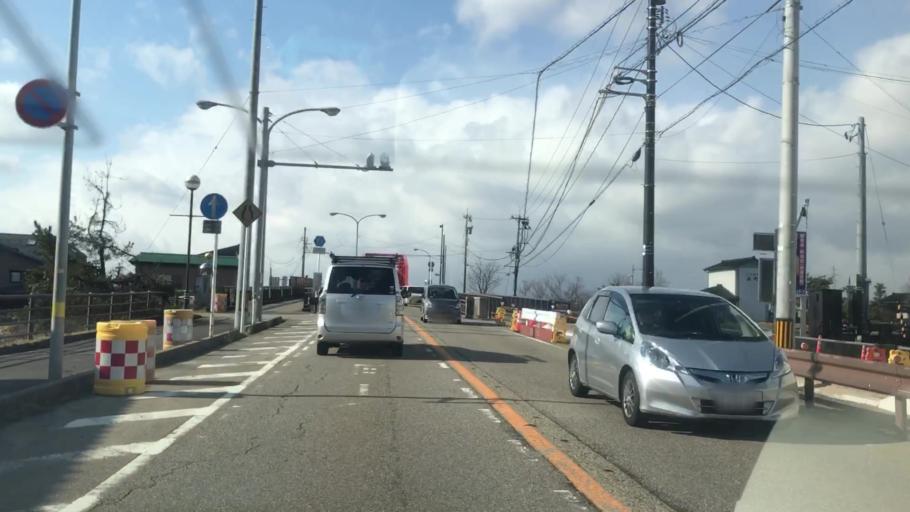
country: JP
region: Toyama
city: Takaoka
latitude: 36.7343
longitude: 137.0467
